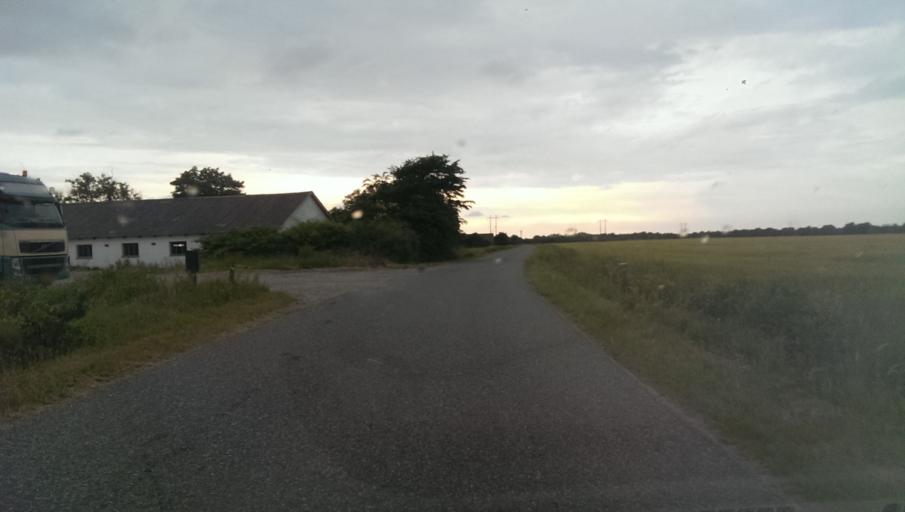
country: DK
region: South Denmark
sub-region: Esbjerg Kommune
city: Bramming
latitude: 55.4350
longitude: 8.7049
